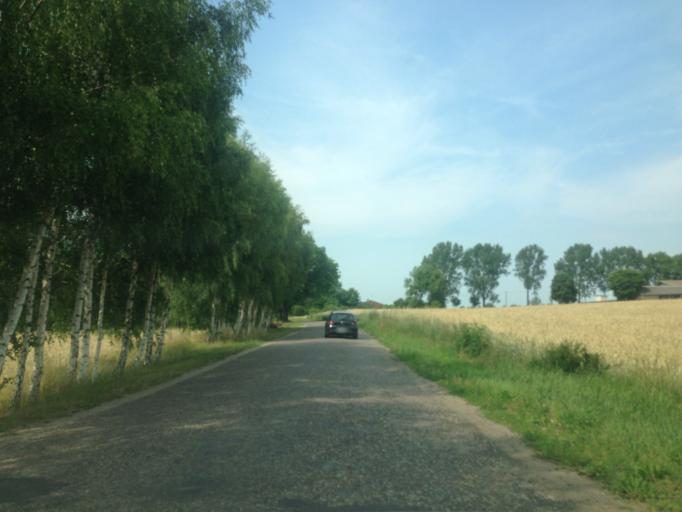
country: PL
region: Kujawsko-Pomorskie
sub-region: Powiat brodnicki
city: Bobrowo
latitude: 53.2439
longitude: 19.2589
